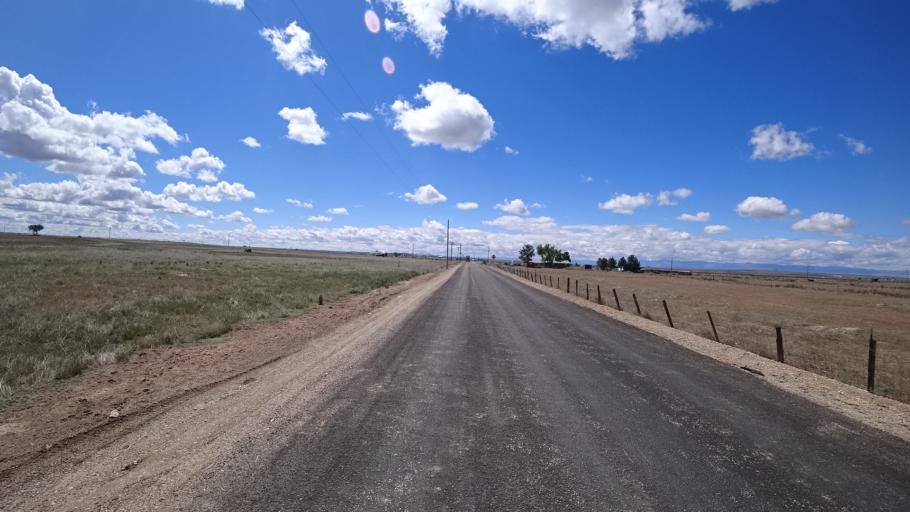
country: US
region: Idaho
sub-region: Ada County
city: Kuna
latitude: 43.4611
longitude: -116.2744
